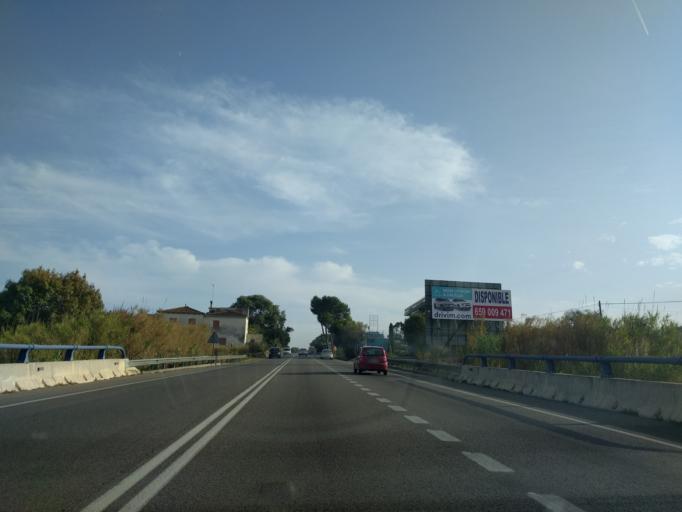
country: ES
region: Catalonia
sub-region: Provincia de Barcelona
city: Tordera
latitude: 41.6913
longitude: 2.7228
